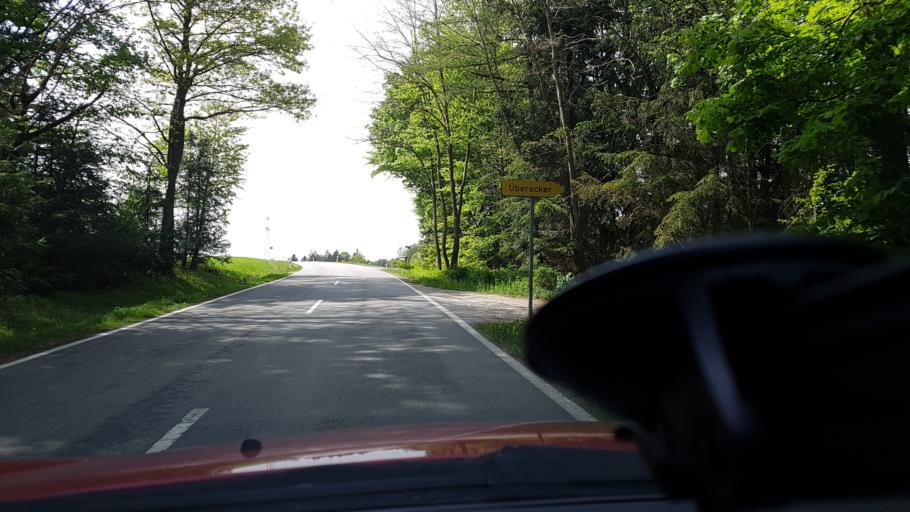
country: DE
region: Bavaria
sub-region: Lower Bavaria
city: Stubenberg
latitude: 48.3465
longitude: 13.0696
